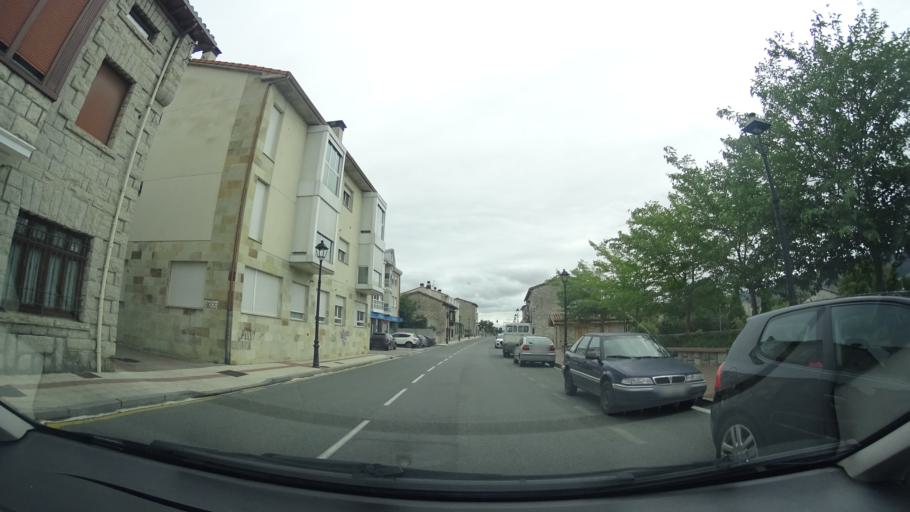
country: ES
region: Basque Country
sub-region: Provincia de Alava
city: Arminon
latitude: 42.8174
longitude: -2.8108
